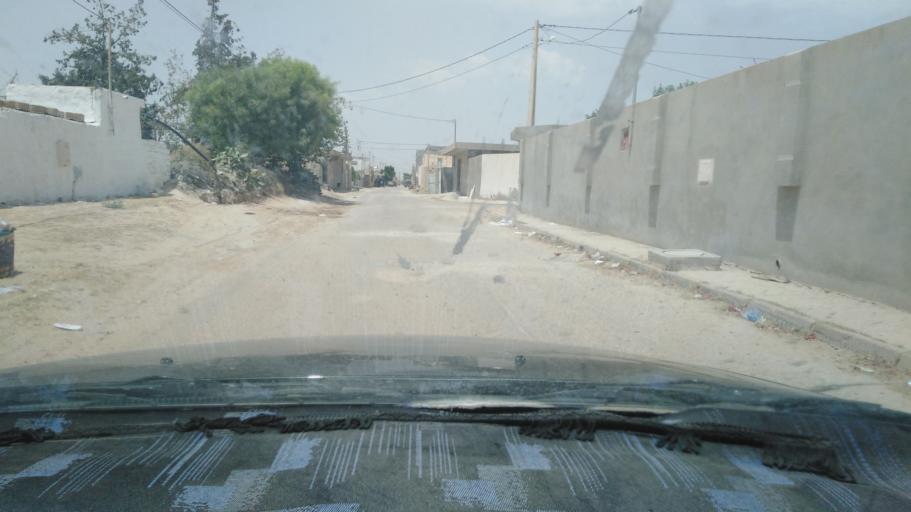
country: TN
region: Qabis
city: Matmata
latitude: 33.6173
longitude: 10.2737
